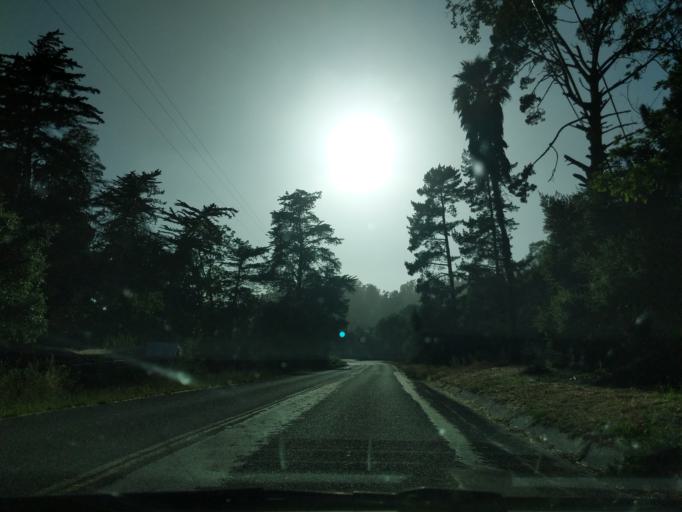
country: US
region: California
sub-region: Monterey County
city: Prunedale
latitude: 36.8252
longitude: -121.6610
